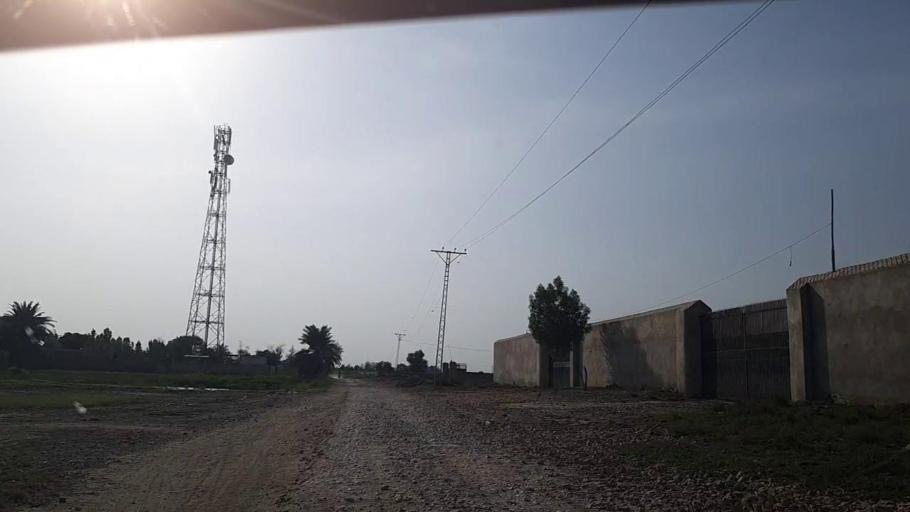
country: PK
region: Sindh
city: Ghotki
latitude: 28.0162
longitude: 69.2939
